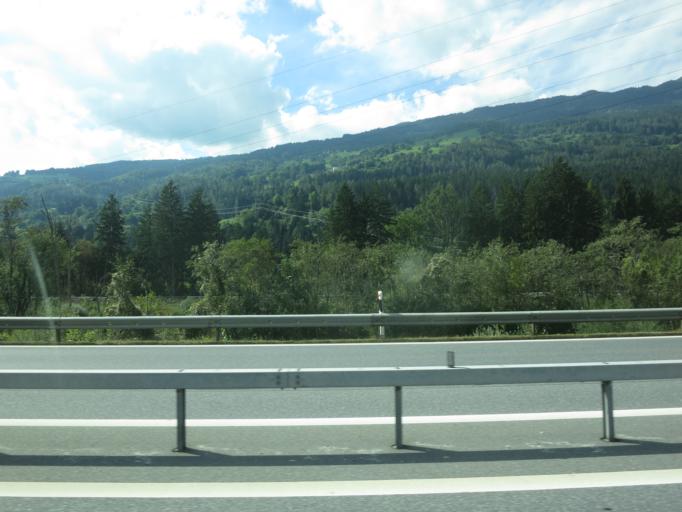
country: CH
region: Grisons
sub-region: Hinterrhein District
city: Cazis
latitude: 46.7480
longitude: 9.4301
